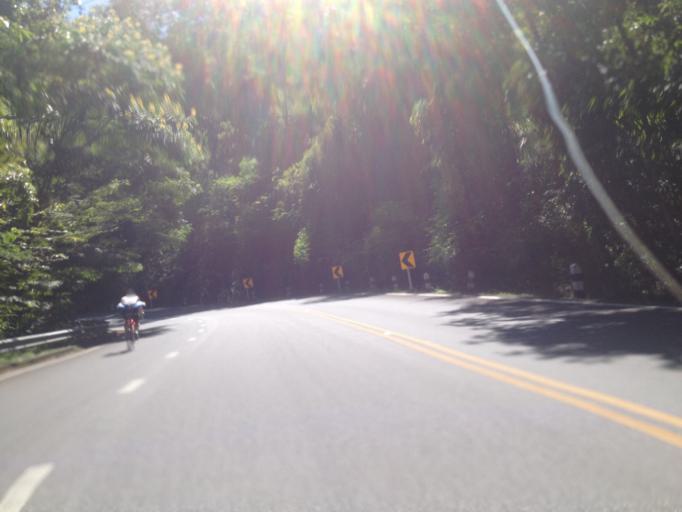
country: TH
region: Chiang Mai
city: Chiang Mai
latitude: 18.8126
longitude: 98.9376
